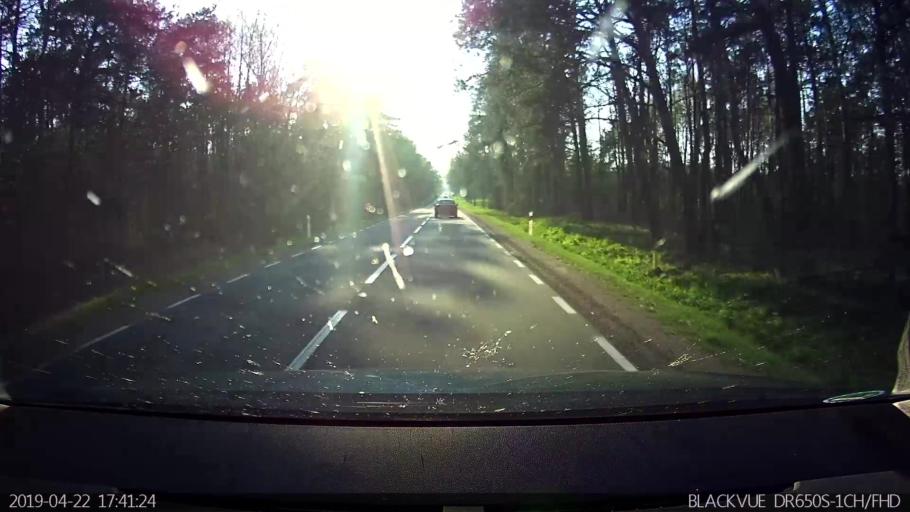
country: PL
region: Masovian Voivodeship
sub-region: Powiat wegrowski
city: Miedzna
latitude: 52.4022
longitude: 22.1073
